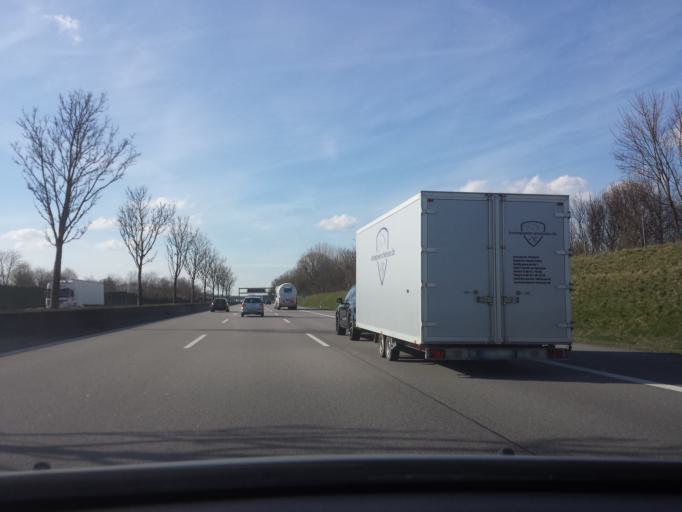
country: DE
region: Bavaria
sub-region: Upper Bavaria
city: Grobenzell
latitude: 48.2268
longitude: 11.3599
